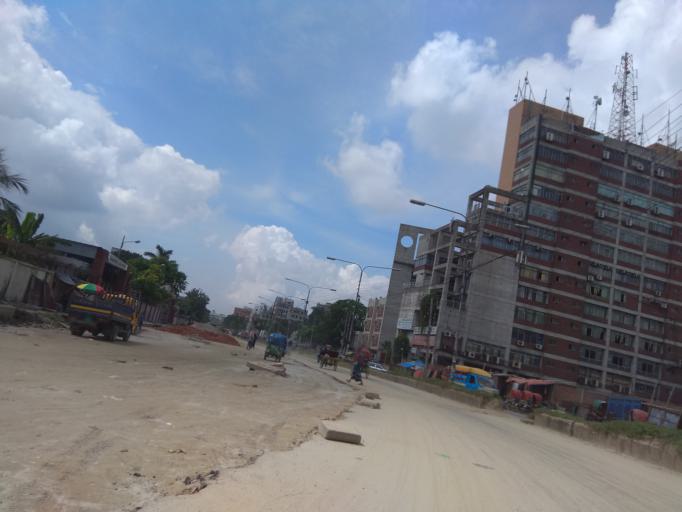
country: BD
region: Dhaka
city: Paltan
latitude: 23.8047
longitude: 90.3877
